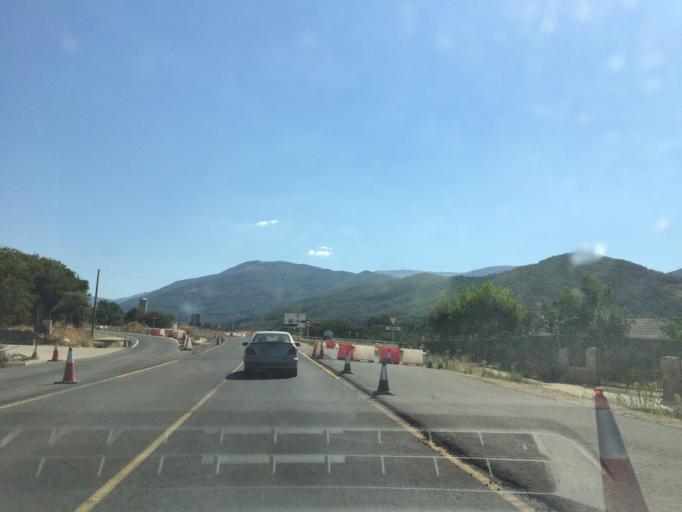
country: ES
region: Extremadura
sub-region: Provincia de Caceres
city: Cabezuela del Valle
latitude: 40.2074
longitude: -5.7818
